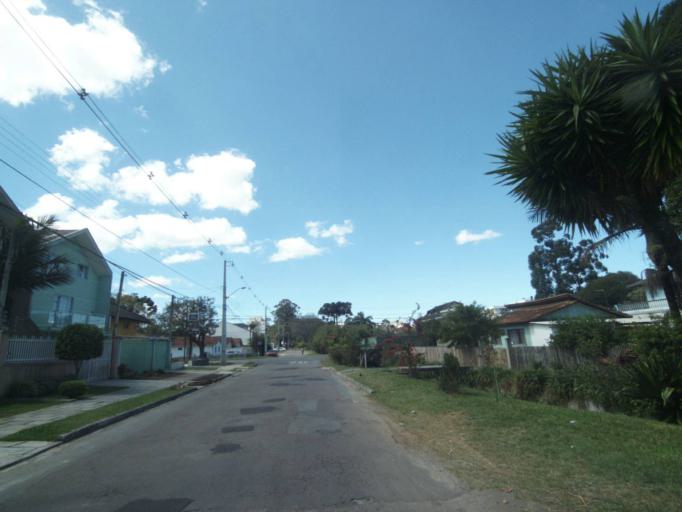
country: BR
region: Parana
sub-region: Curitiba
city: Curitiba
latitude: -25.3884
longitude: -49.2423
